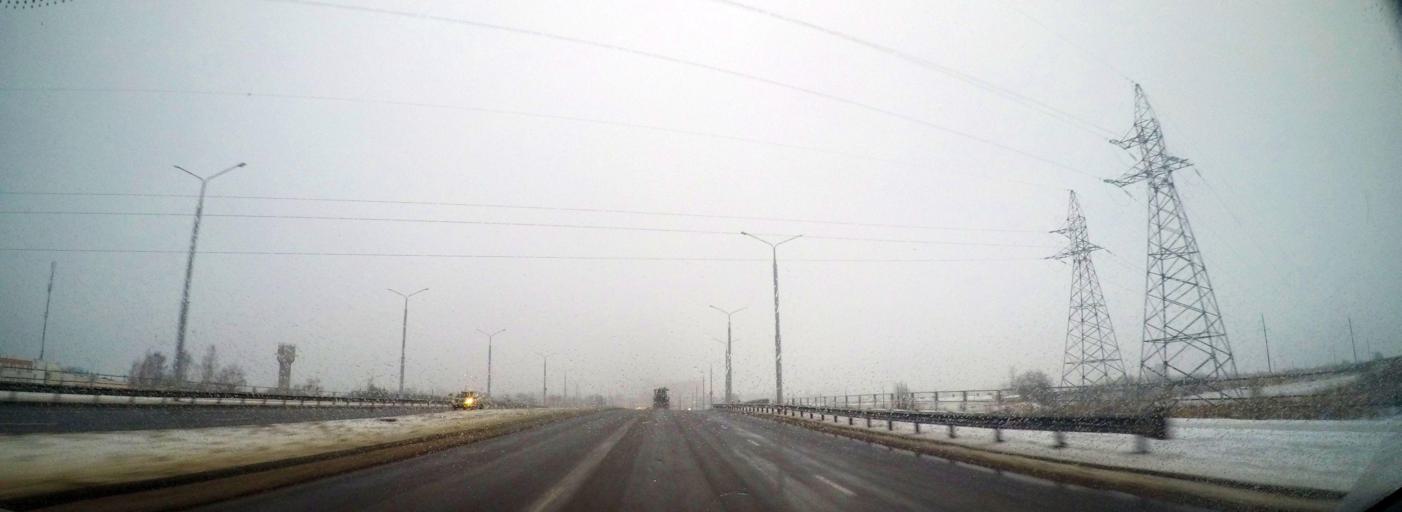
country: BY
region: Grodnenskaya
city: Hrodna
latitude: 53.6345
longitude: 23.8090
